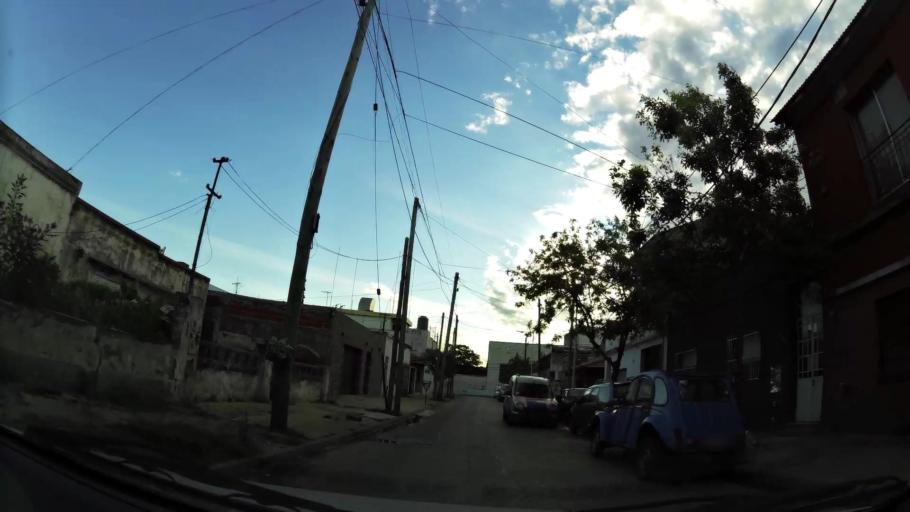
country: AR
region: Buenos Aires
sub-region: Partido de Avellaneda
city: Avellaneda
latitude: -34.6923
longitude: -58.3509
